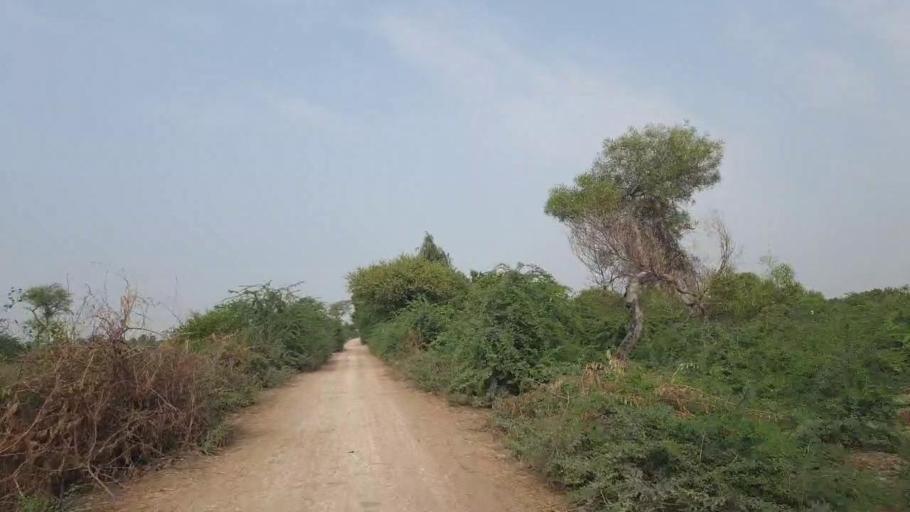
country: PK
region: Sindh
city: Badin
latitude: 24.5961
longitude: 68.7413
